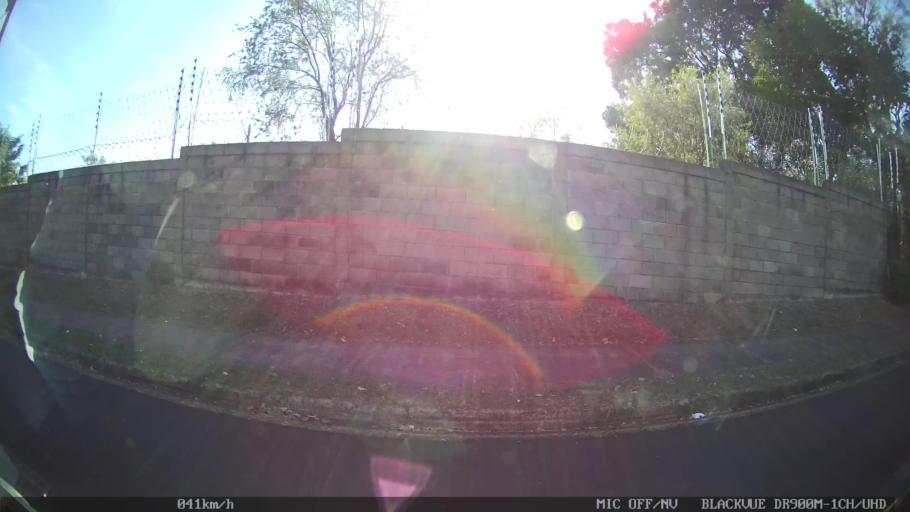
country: BR
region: Sao Paulo
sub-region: Sao Jose Do Rio Preto
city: Sao Jose do Rio Preto
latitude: -20.7784
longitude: -49.3441
